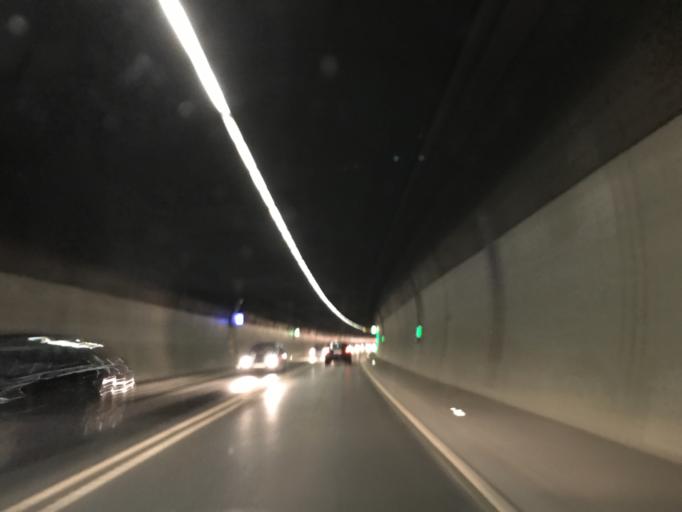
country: DE
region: Baden-Wuerttemberg
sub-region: Regierungsbezirk Stuttgart
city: Stuttgart
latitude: 48.7584
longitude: 9.1666
